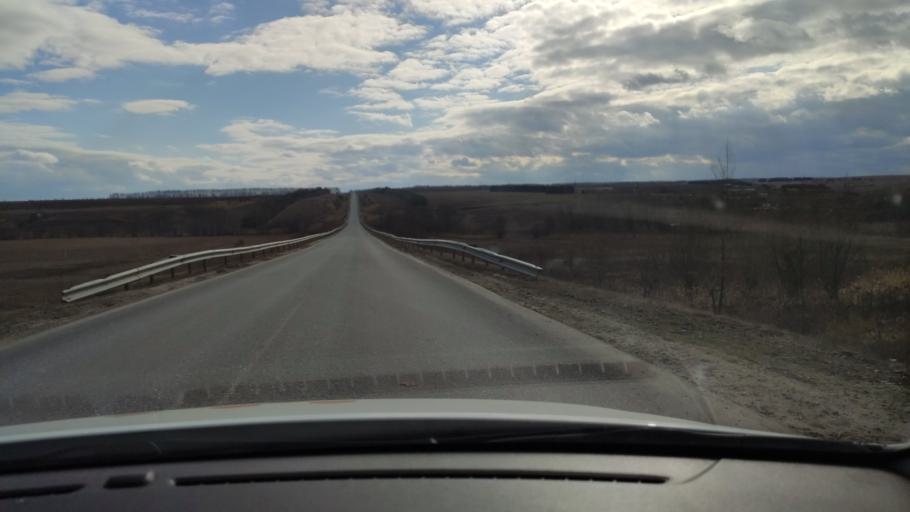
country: RU
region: Tatarstan
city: Vysokaya Gora
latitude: 56.0257
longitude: 49.2068
